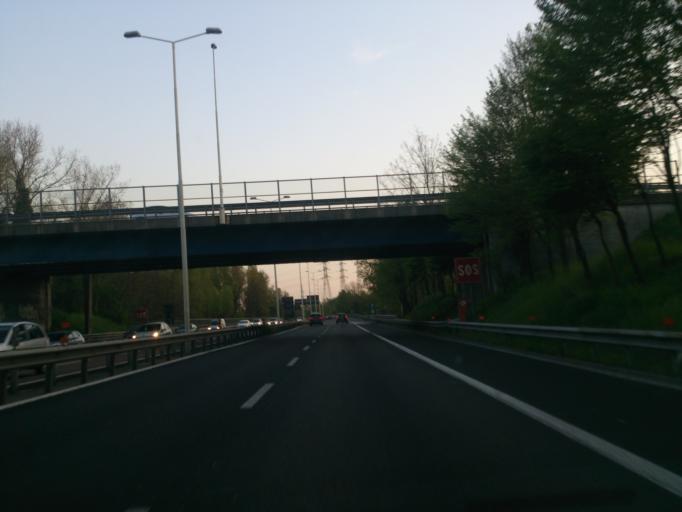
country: IT
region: Lombardy
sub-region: Citta metropolitana di Milano
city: Cologno Monzese
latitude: 45.5474
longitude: 9.2602
